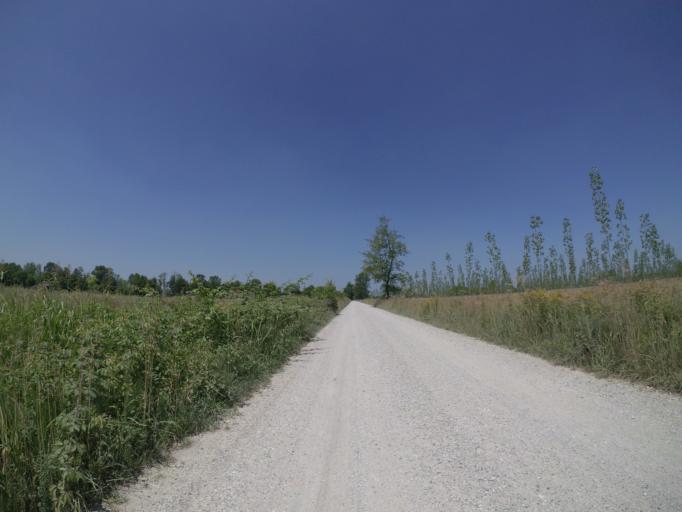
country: IT
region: Friuli Venezia Giulia
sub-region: Provincia di Udine
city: Bertiolo
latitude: 45.9349
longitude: 13.0184
